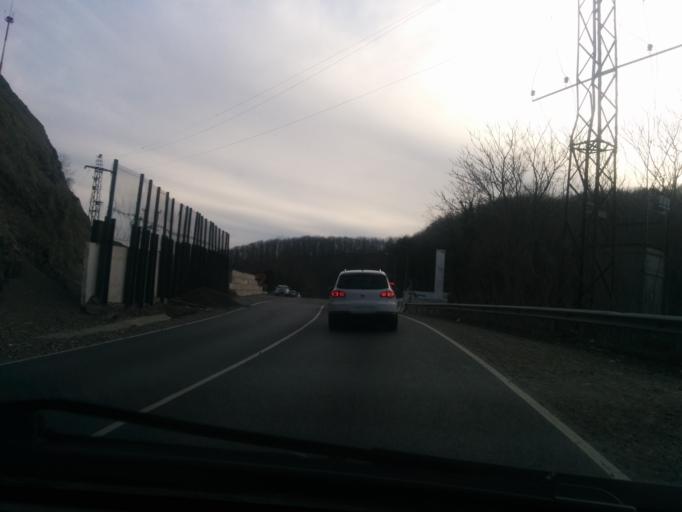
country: RU
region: Krasnodarskiy
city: Agoy
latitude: 44.1330
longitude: 39.0483
